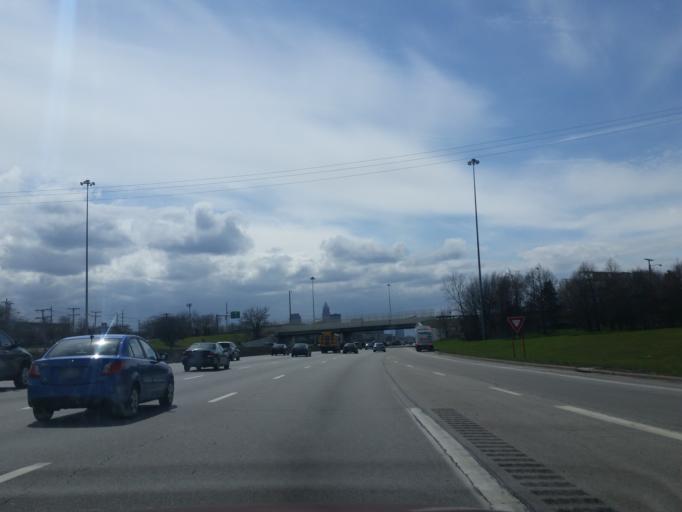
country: US
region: Ohio
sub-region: Cuyahoga County
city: Bratenahl
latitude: 41.5314
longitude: -81.6501
